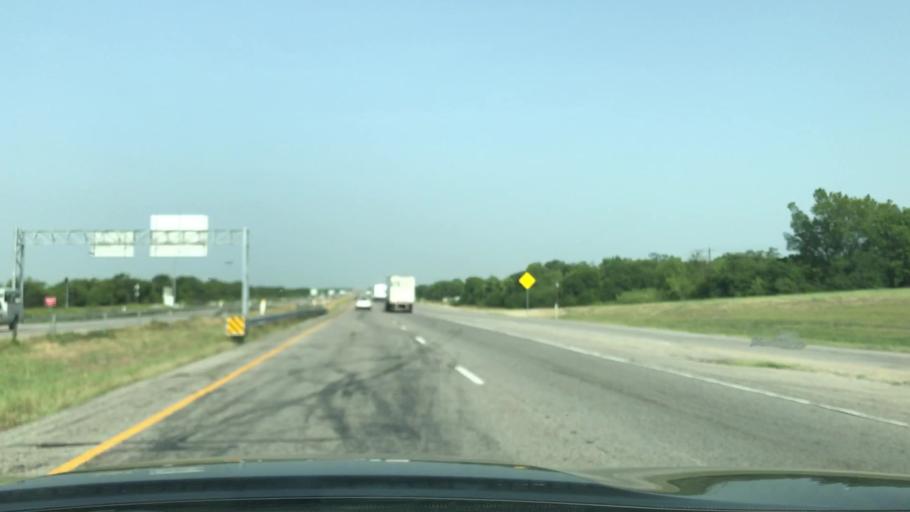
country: US
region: Texas
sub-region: Kaufman County
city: Talty
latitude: 32.7392
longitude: -96.3716
